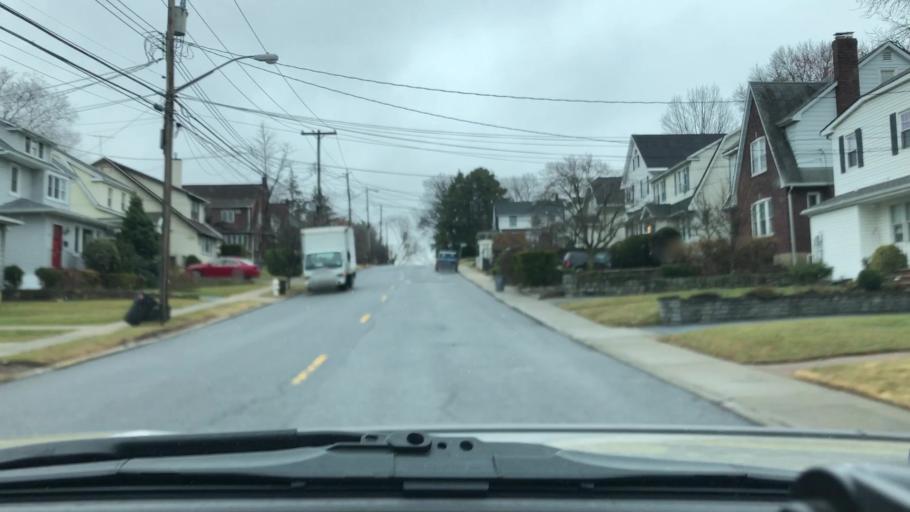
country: US
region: New Jersey
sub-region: Hudson County
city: Bayonne
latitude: 40.6258
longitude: -74.1048
